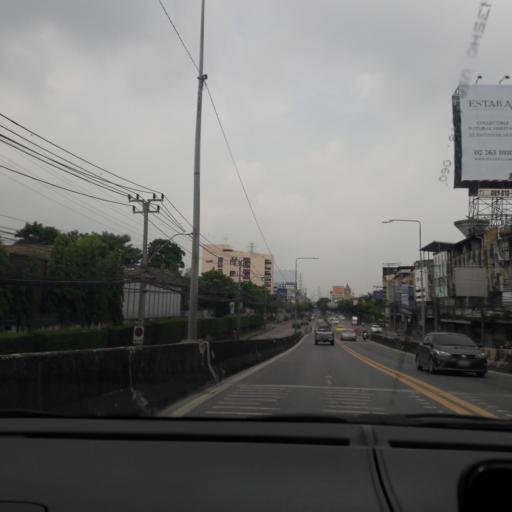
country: TH
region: Bangkok
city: Suan Luang
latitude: 13.7358
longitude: 100.6393
